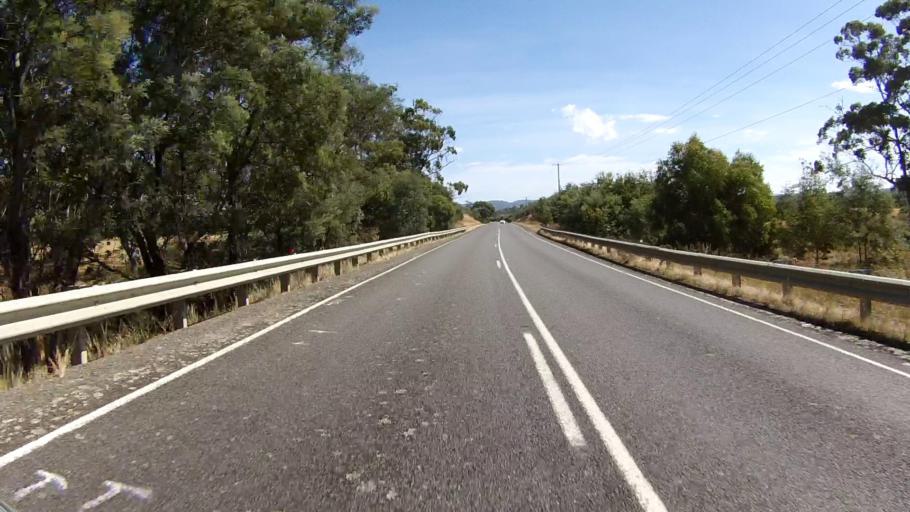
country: AU
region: Tasmania
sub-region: Sorell
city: Sorell
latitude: -42.5926
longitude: 147.7950
